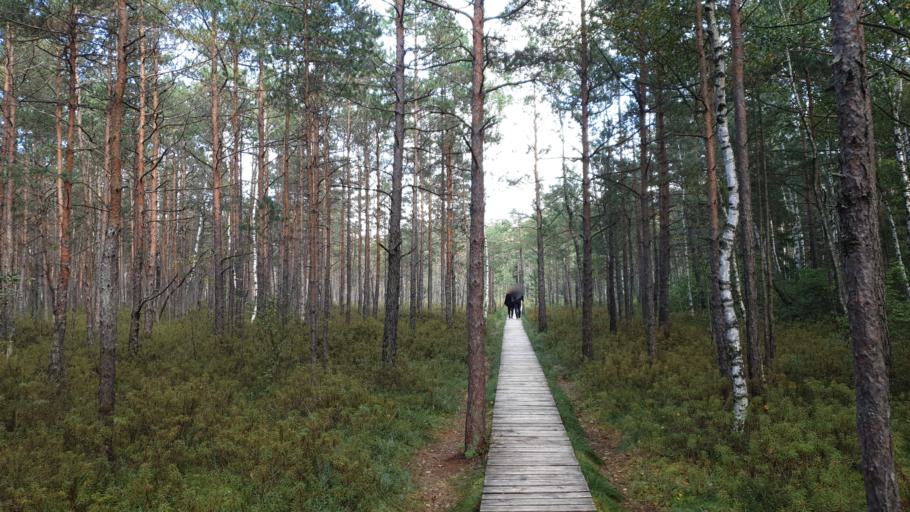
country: LT
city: Trakai
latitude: 54.6381
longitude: 24.9711
